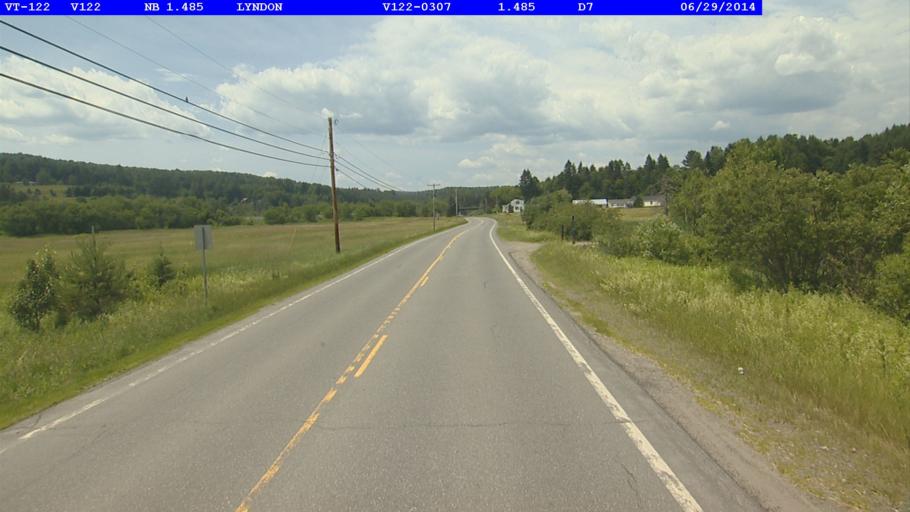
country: US
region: Vermont
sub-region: Caledonia County
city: Lyndonville
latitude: 44.5512
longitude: -72.0239
